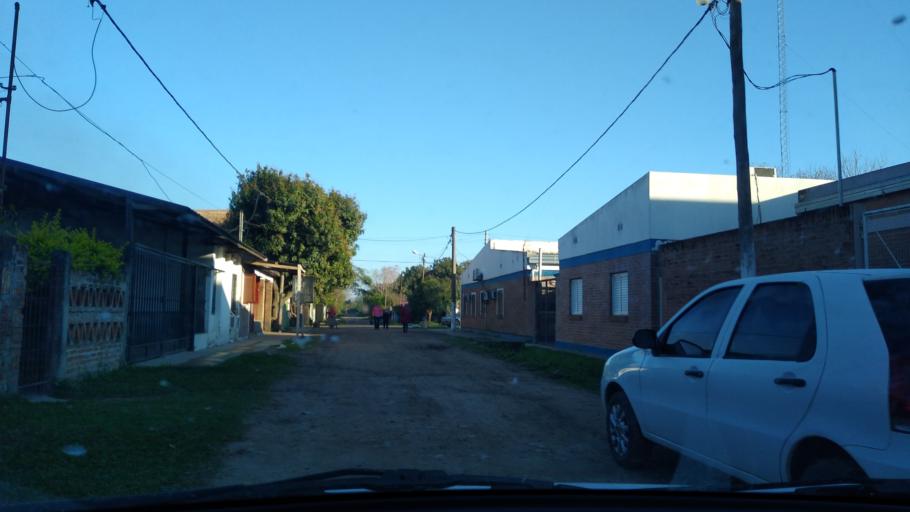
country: AR
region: Chaco
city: Resistencia
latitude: -27.4855
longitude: -58.9703
